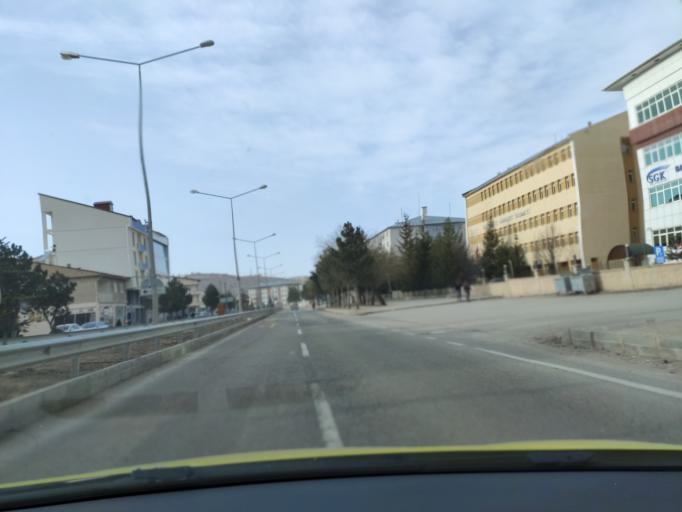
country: TR
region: Bayburt
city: Bayburt
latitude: 40.2465
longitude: 40.2335
